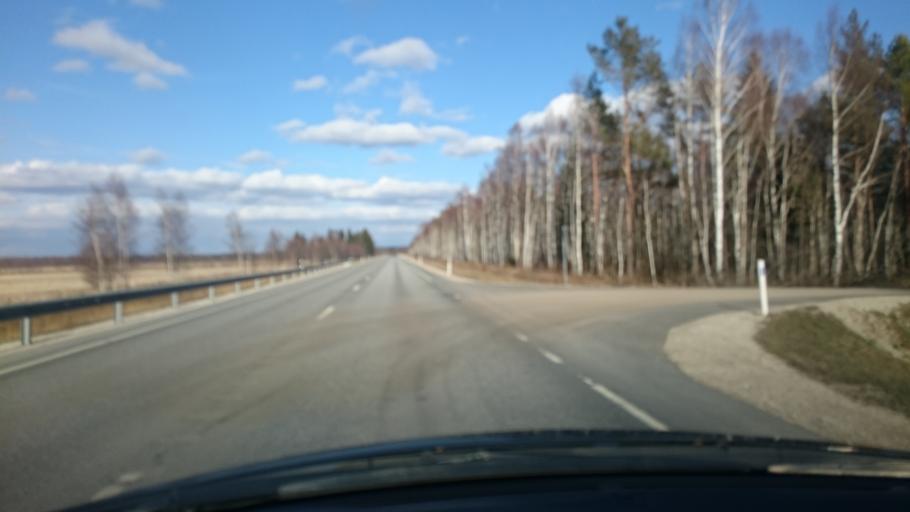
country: EE
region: Laeaene
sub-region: Lihula vald
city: Lihula
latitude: 58.7880
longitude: 24.0218
